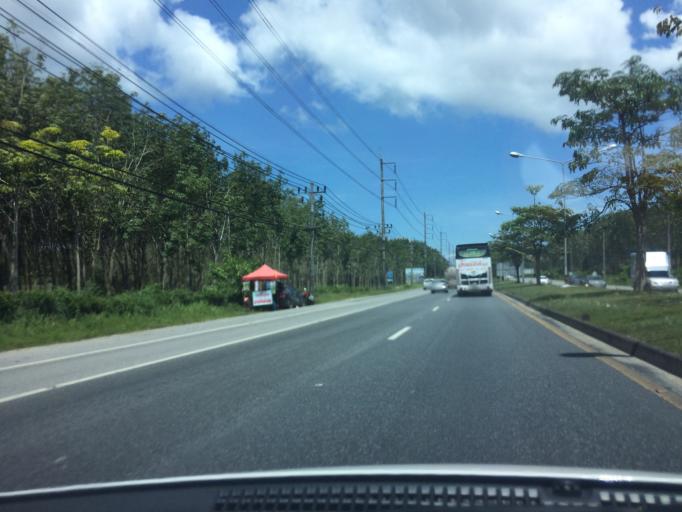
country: TH
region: Phuket
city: Thalang
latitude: 8.0533
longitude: 98.3385
